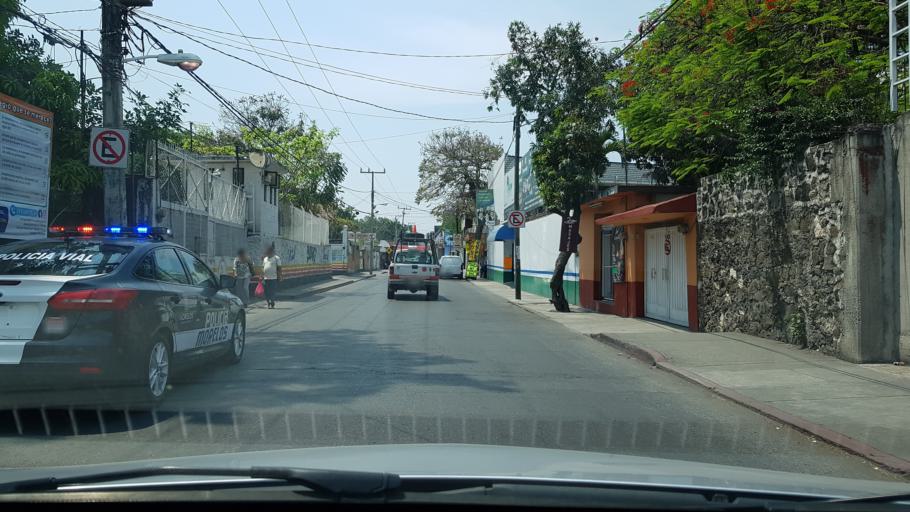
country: MX
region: Morelos
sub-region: Jiutepec
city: Jiutepec
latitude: 18.8850
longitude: -99.1772
